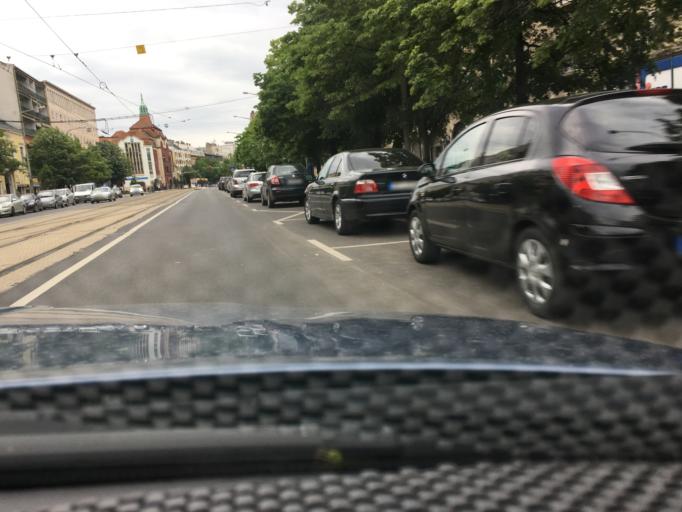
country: HU
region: Hajdu-Bihar
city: Debrecen
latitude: 47.5282
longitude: 21.6256
